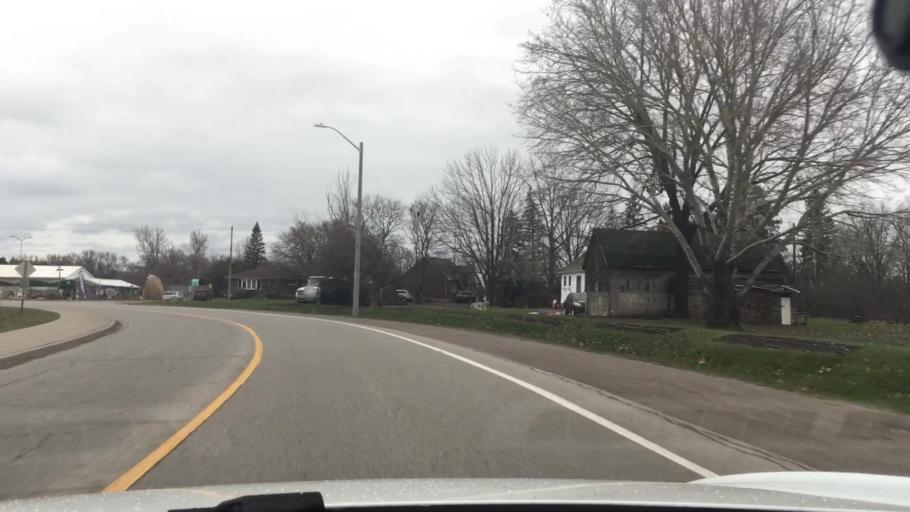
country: CA
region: Ontario
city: Oshawa
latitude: 43.8887
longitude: -78.8234
